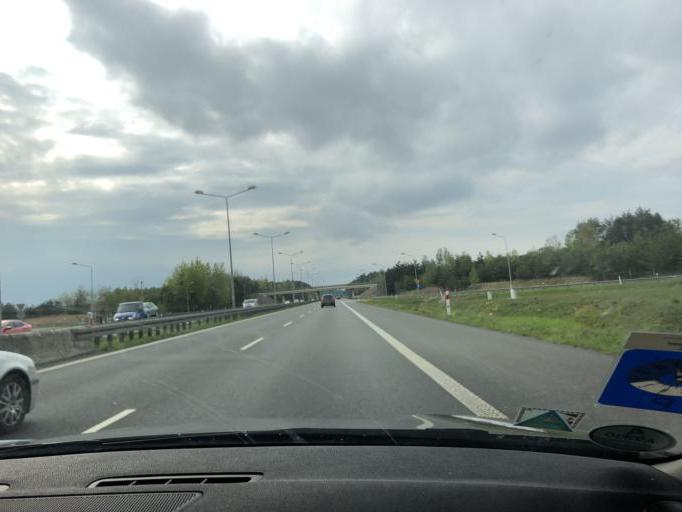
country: PL
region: Opole Voivodeship
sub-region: Powiat opolski
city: Dabrowa
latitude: 50.6610
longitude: 17.6989
